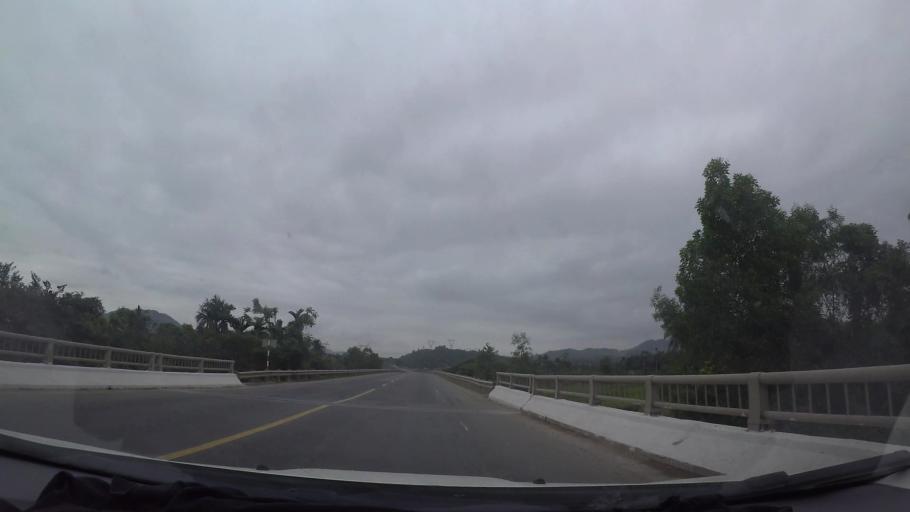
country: VN
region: Da Nang
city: Lien Chieu
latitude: 16.0774
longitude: 108.0865
